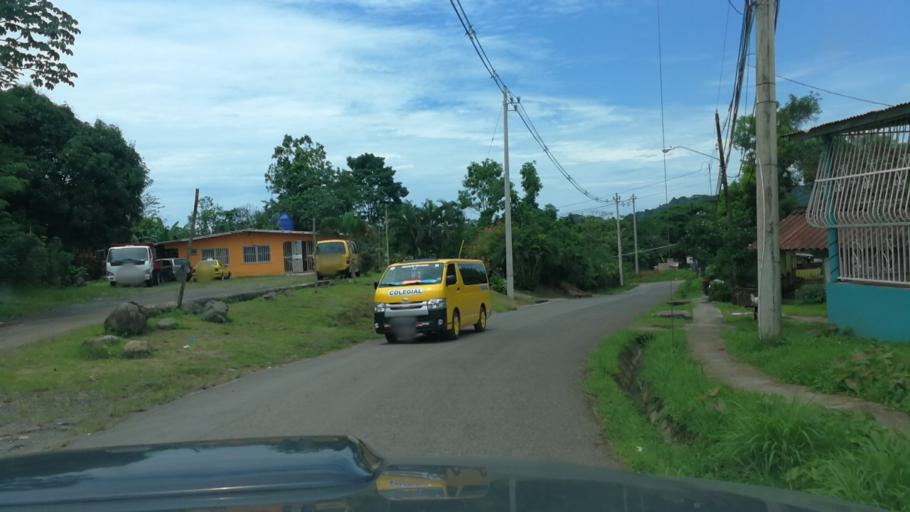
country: PA
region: Panama
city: San Miguelito
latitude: 9.0986
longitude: -79.4560
